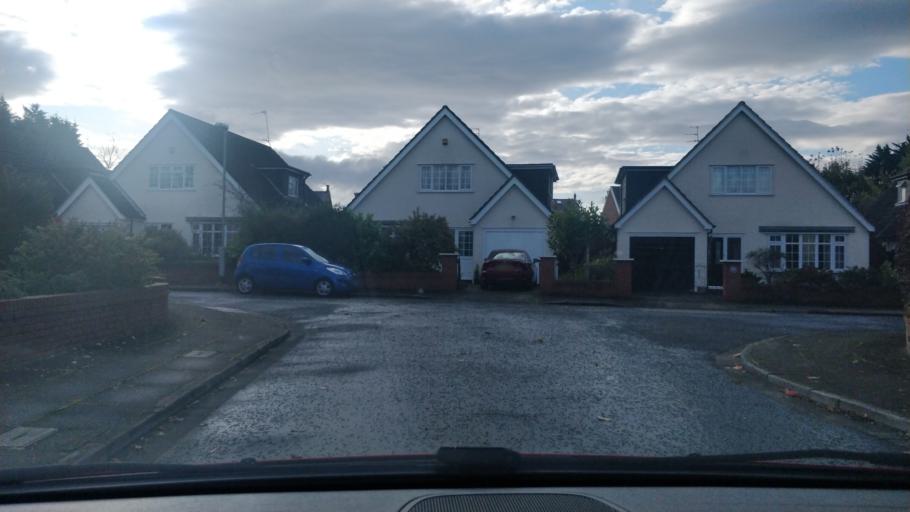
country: GB
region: England
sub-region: Sefton
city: Southport
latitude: 53.6301
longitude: -3.0157
